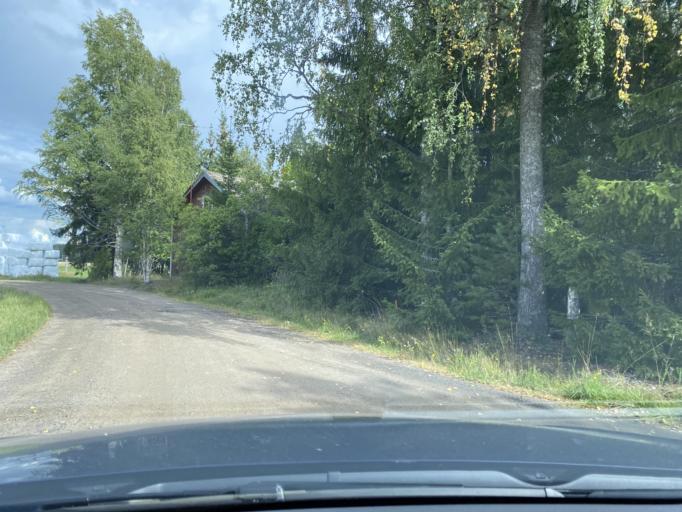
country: FI
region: Haeme
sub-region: Forssa
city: Humppila
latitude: 61.0641
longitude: 23.2749
